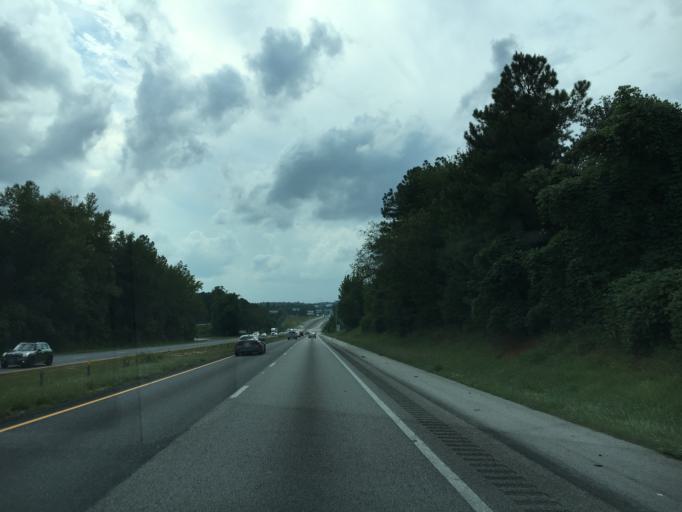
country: US
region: South Carolina
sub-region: Cherokee County
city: Gaffney
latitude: 35.0793
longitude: -81.7167
